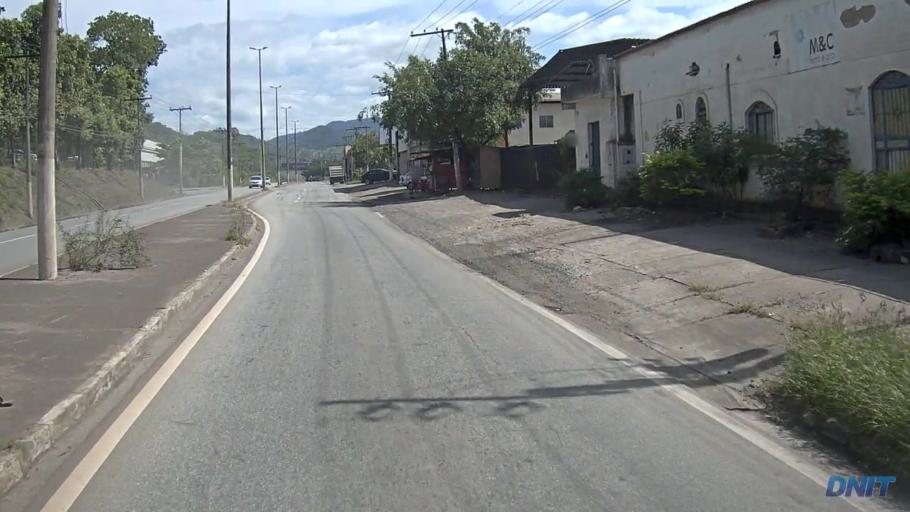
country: BR
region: Minas Gerais
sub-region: Coronel Fabriciano
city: Coronel Fabriciano
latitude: -19.5282
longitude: -42.6459
